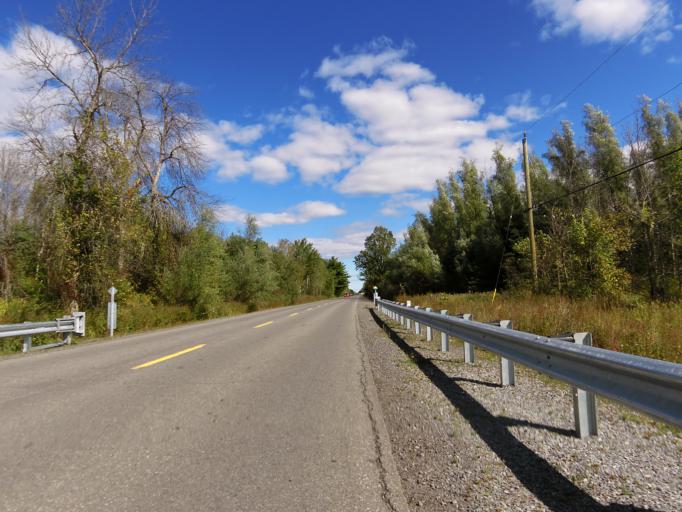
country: CA
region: Ontario
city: Ottawa
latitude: 45.3579
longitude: -75.5391
